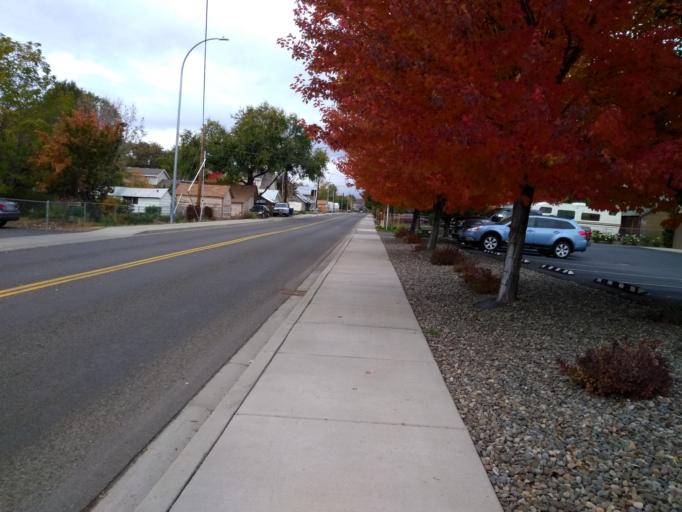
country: US
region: Washington
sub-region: Kittitas County
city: Ellensburg
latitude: 46.9850
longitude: -120.5445
